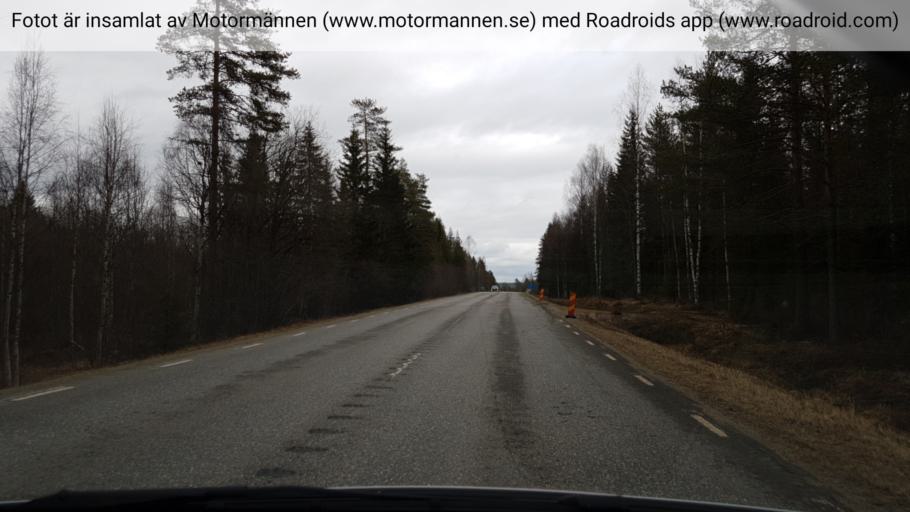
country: SE
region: Vaesterbotten
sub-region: Bjurholms Kommun
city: Bjurholm
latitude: 63.9245
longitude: 19.0922
